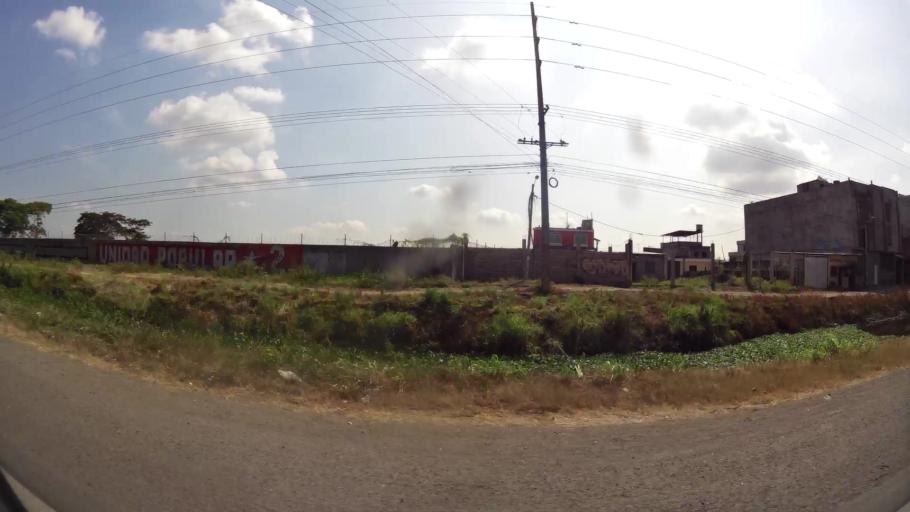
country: EC
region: Guayas
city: Eloy Alfaro
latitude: -2.1821
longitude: -79.8191
